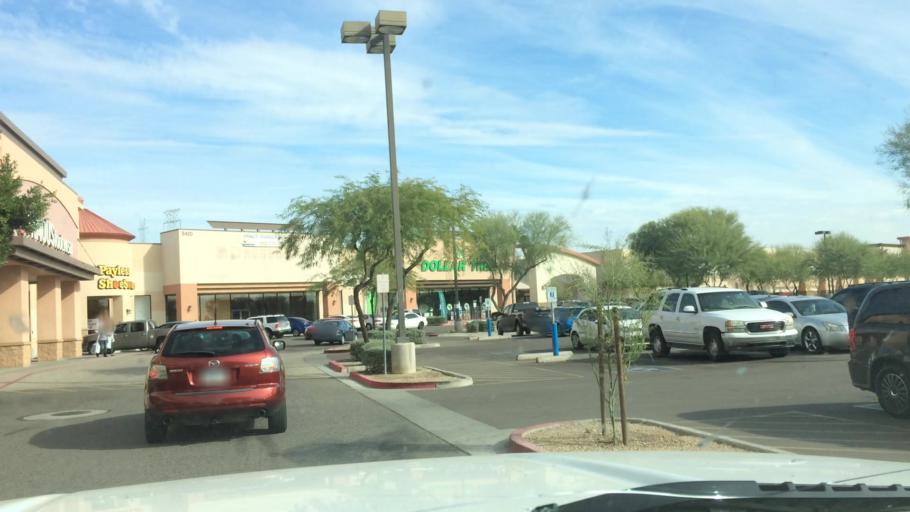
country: US
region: Arizona
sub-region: Maricopa County
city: Peoria
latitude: 33.5536
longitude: -112.2620
